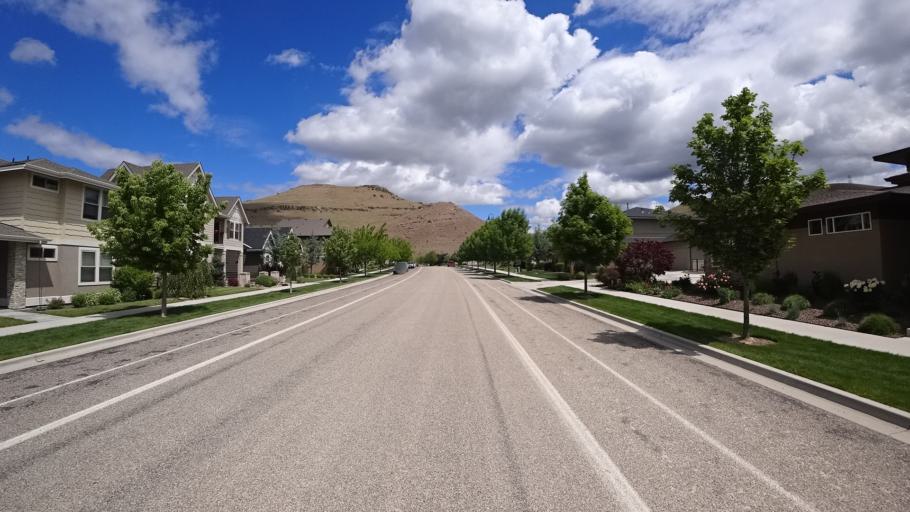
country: US
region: Idaho
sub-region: Ada County
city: Boise
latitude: 43.5780
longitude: -116.1318
